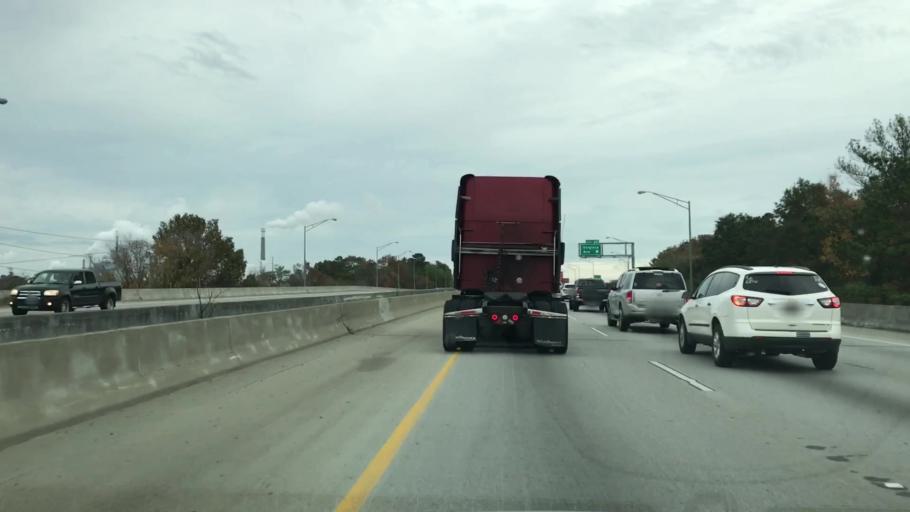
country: US
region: South Carolina
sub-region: Charleston County
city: North Charleston
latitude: 32.8940
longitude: -79.9840
